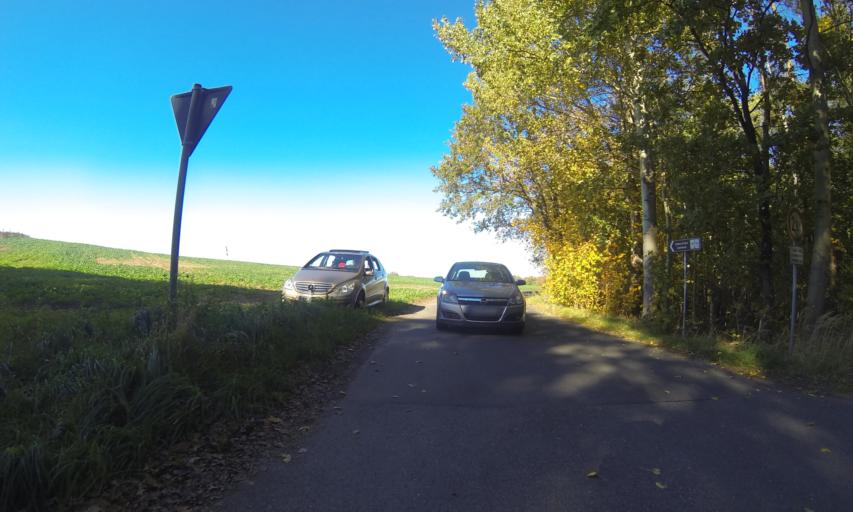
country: DE
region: Saxony
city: Weinbohla
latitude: 51.2017
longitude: 13.5948
